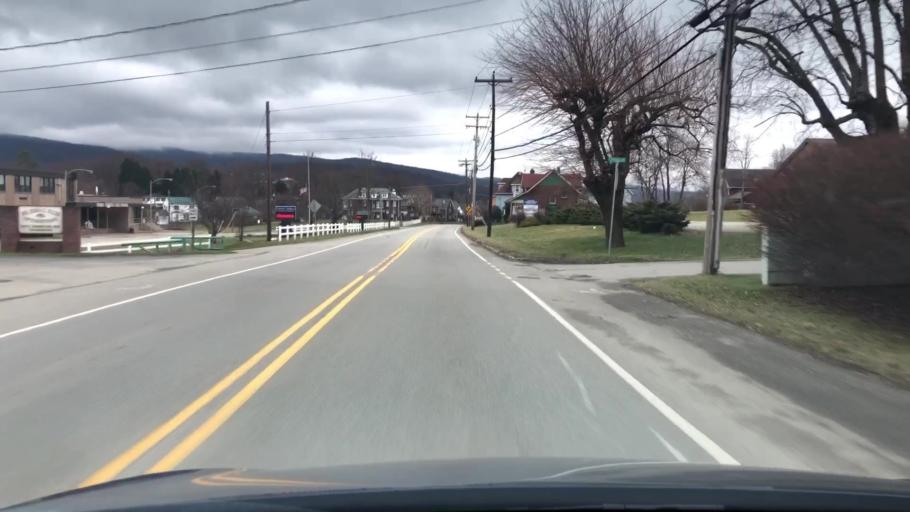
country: US
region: Pennsylvania
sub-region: Fayette County
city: Connellsville
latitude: 40.0274
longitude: -79.5809
